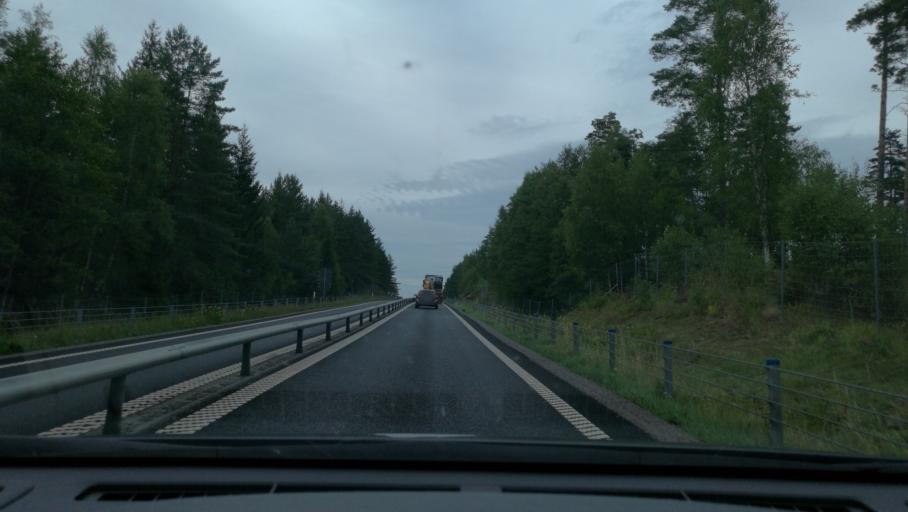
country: SE
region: Soedermanland
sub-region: Katrineholms Kommun
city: Katrineholm
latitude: 58.8928
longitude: 16.2100
